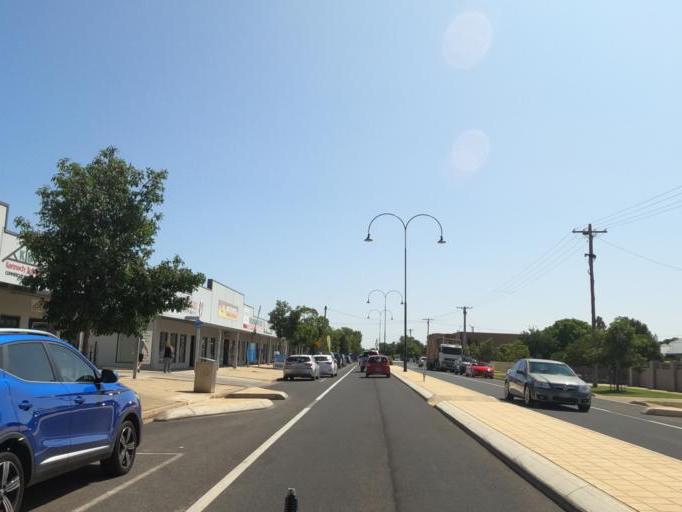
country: AU
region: New South Wales
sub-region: Corowa Shire
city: Mulwala
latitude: -35.9906
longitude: 146.0041
